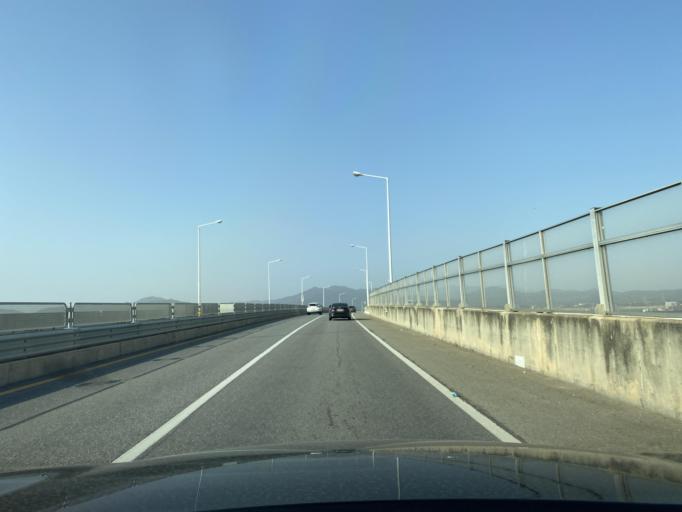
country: KR
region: Chungcheongnam-do
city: Yesan
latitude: 36.6912
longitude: 126.7394
